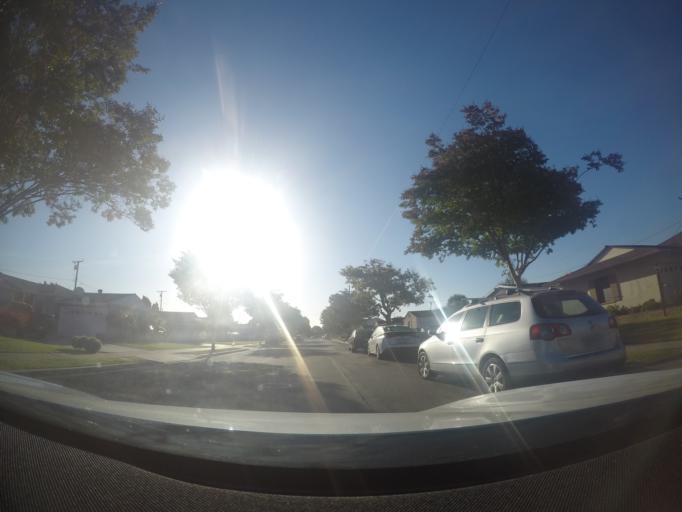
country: US
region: California
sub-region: Los Angeles County
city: Lawndale
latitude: 33.8641
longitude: -118.3459
